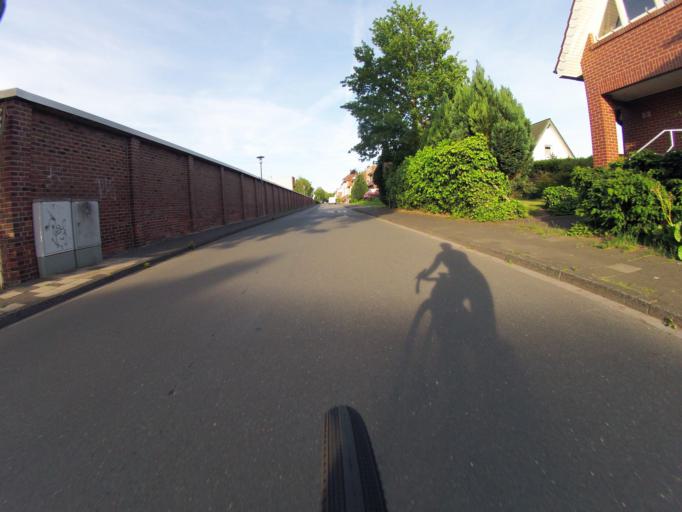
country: DE
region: North Rhine-Westphalia
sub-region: Regierungsbezirk Munster
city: Tecklenburg
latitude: 52.2606
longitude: 7.7846
